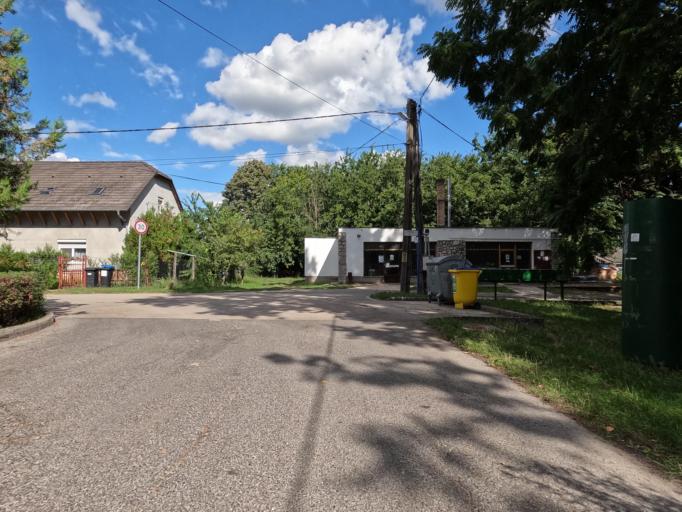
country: HU
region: Tolna
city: Paks
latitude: 46.5909
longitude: 18.8095
